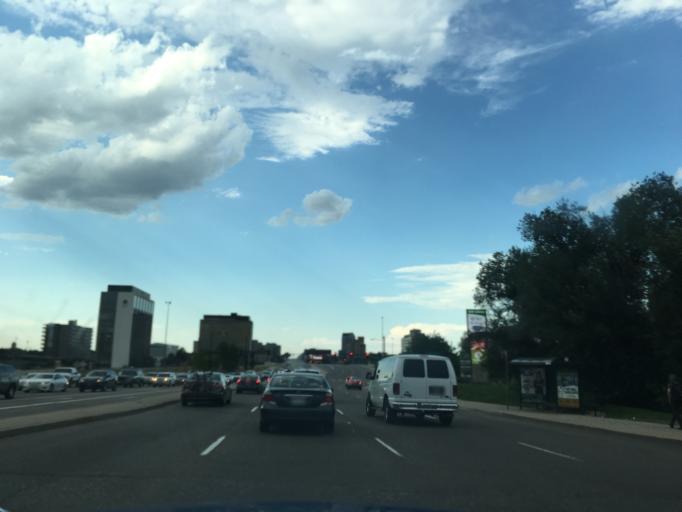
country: US
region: Colorado
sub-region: Arapahoe County
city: Glendale
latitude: 39.6801
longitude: -104.9407
